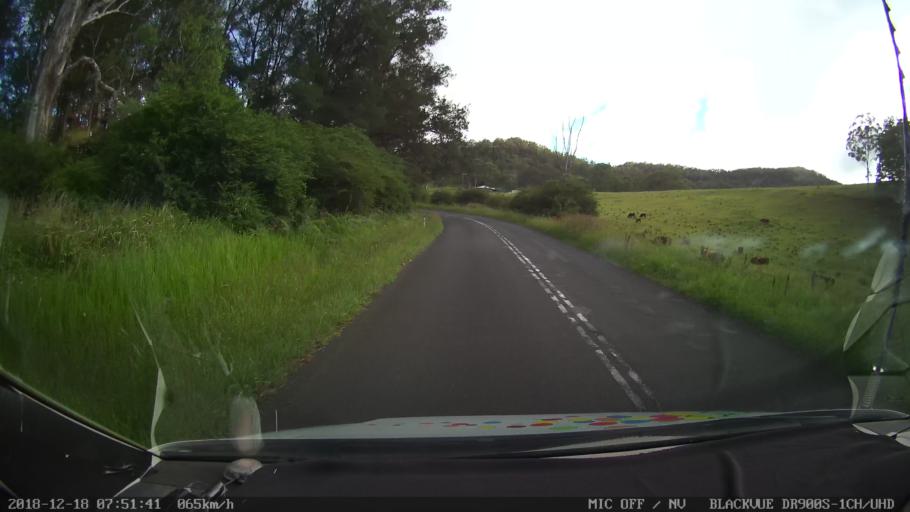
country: AU
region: New South Wales
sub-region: Kyogle
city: Kyogle
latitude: -28.4358
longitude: 152.5802
